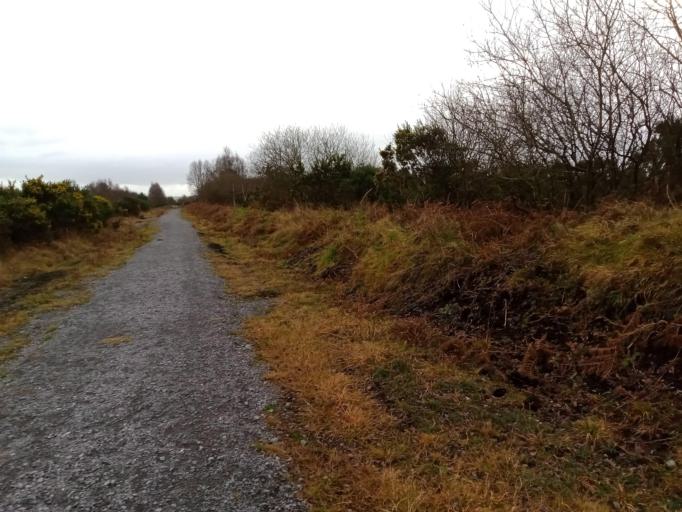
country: IE
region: Munster
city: Thurles
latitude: 52.5948
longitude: -7.7436
